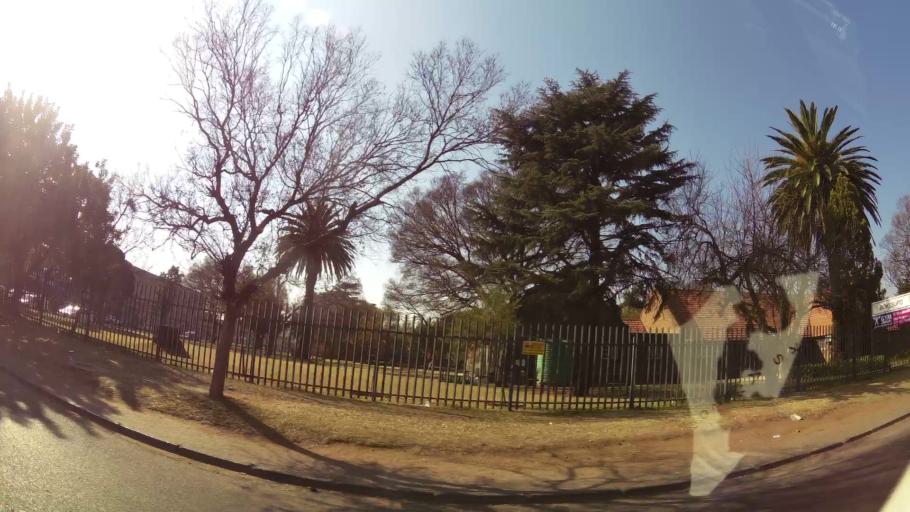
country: ZA
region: Gauteng
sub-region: Ekurhuleni Metropolitan Municipality
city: Boksburg
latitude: -26.2244
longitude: 28.2531
